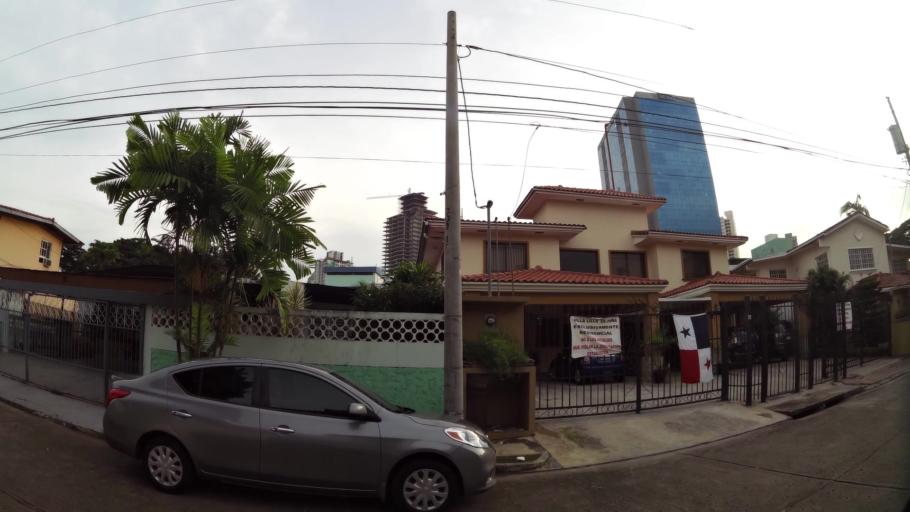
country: PA
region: Panama
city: Panama
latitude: 8.9914
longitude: -79.5159
